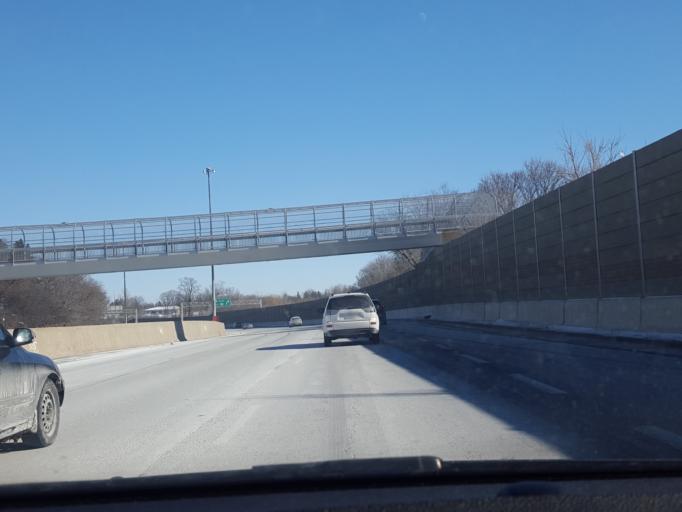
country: CA
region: Ontario
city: Kitchener
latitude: 43.4309
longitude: -80.4642
